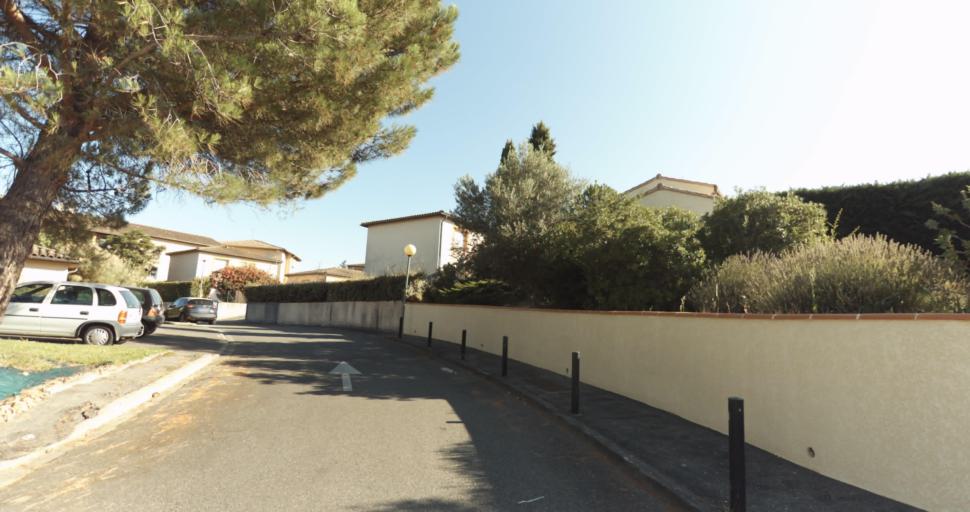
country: FR
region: Midi-Pyrenees
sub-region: Departement de la Haute-Garonne
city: L'Union
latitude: 43.6640
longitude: 1.4824
